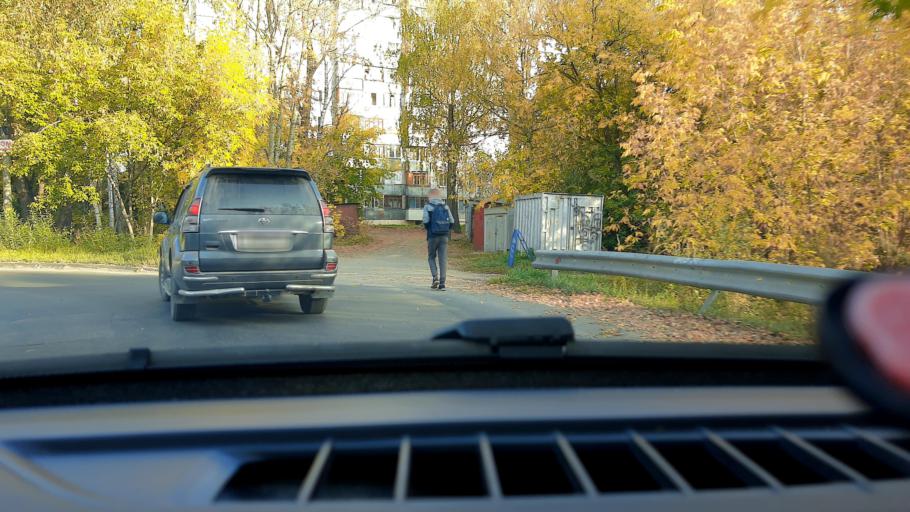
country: RU
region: Nizjnij Novgorod
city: Gorbatovka
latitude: 56.3394
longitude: 43.8306
